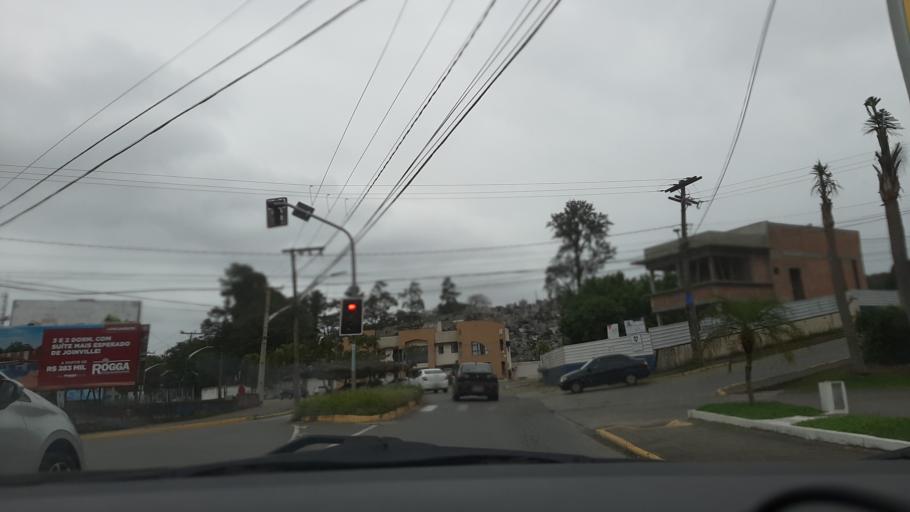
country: BR
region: Santa Catarina
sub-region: Joinville
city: Joinville
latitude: -26.3108
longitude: -48.8555
